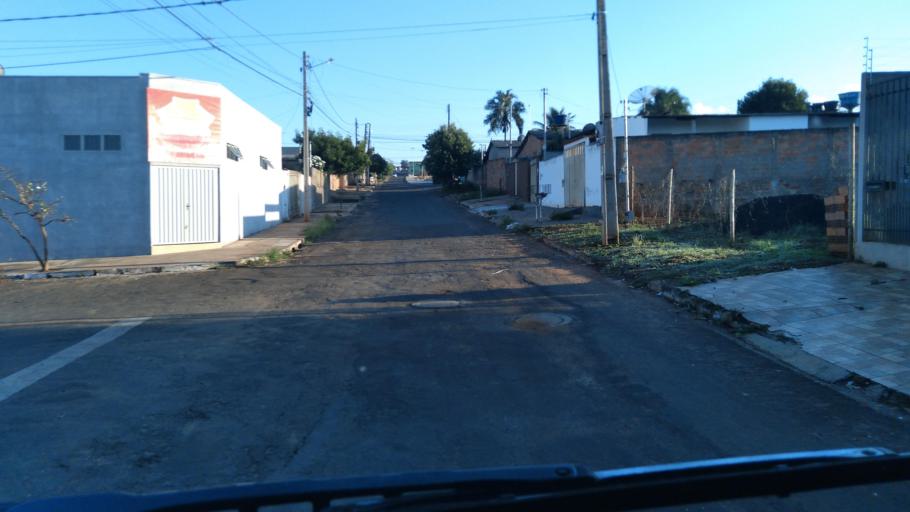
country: BR
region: Goias
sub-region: Mineiros
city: Mineiros
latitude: -17.5739
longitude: -52.5701
